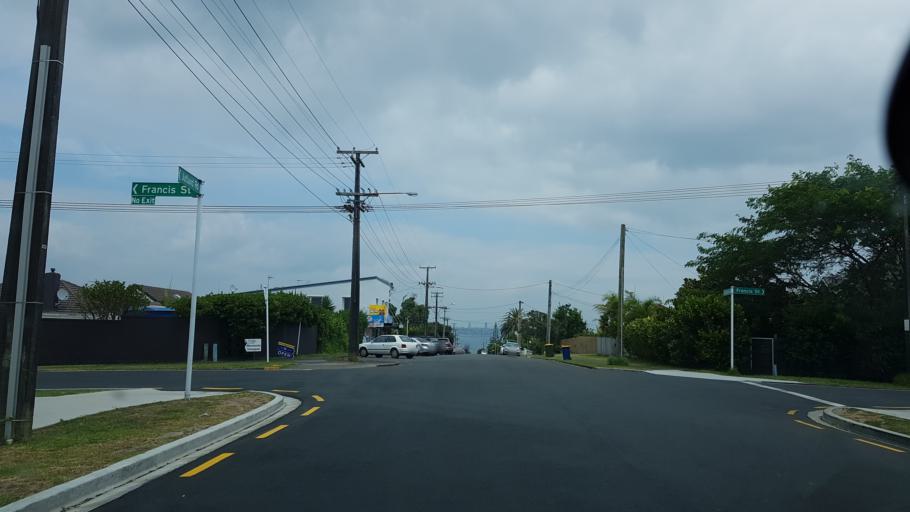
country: NZ
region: Auckland
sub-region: Auckland
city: North Shore
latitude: -36.8012
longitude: 174.7759
